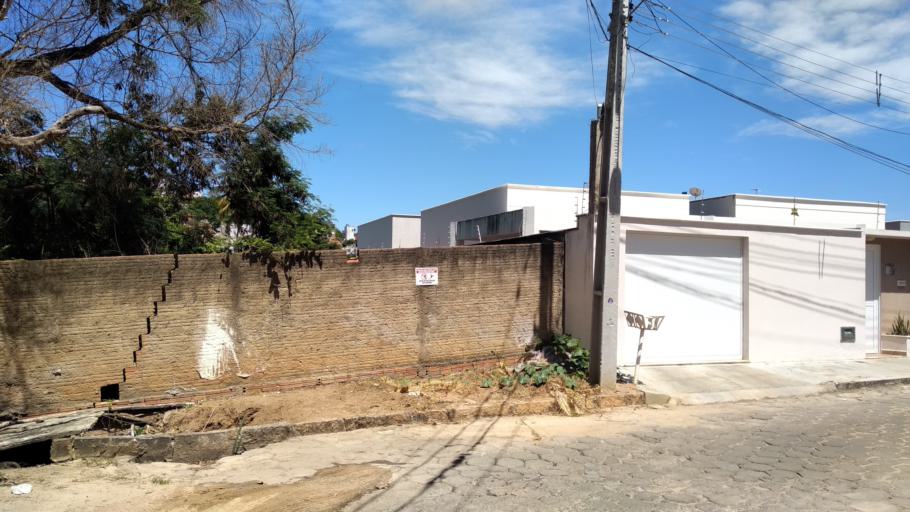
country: BR
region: Bahia
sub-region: Caetite
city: Caetite
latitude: -14.0740
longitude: -42.4830
